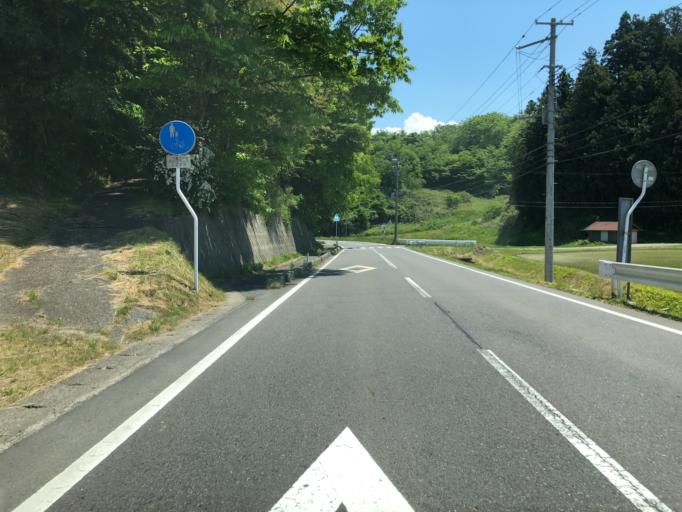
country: JP
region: Fukushima
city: Funehikimachi-funehiki
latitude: 37.4888
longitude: 140.5313
